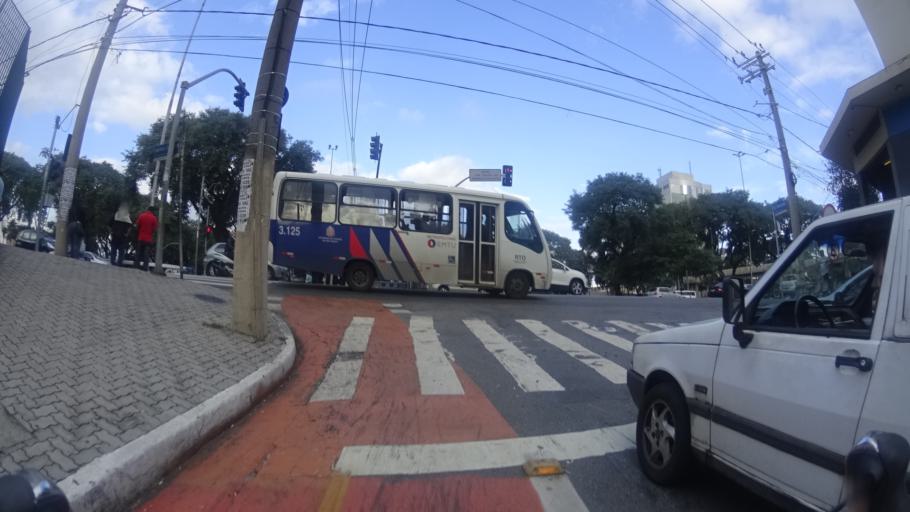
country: BR
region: Sao Paulo
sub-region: Sao Paulo
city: Sao Paulo
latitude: -23.5260
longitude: -46.6315
